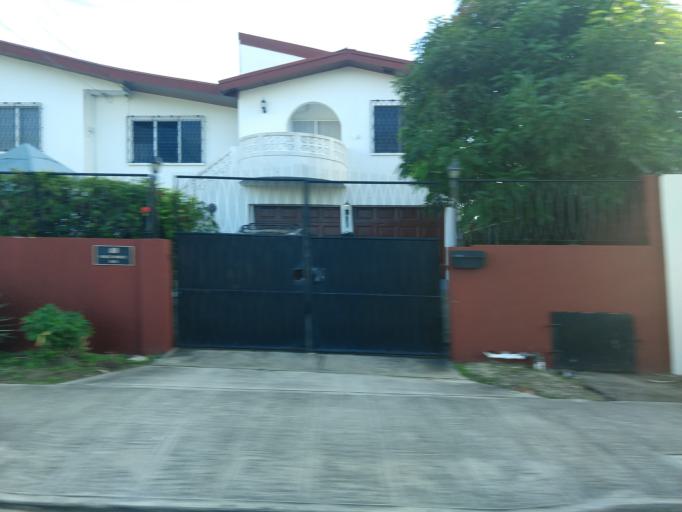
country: BZ
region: Belize
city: Belize City
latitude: 17.5120
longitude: -88.1932
